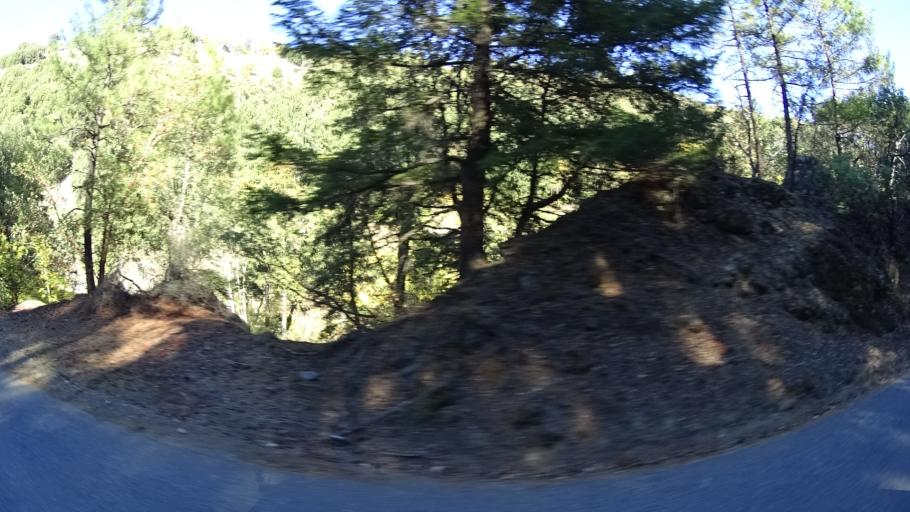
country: US
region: California
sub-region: Humboldt County
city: Willow Creek
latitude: 41.2559
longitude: -123.3184
